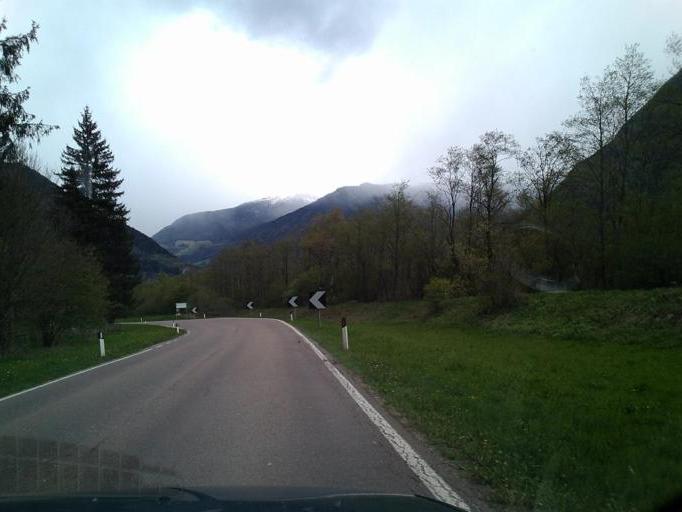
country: IT
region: Trentino-Alto Adige
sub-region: Bolzano
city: Molini di Tures
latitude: 46.8849
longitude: 11.9469
